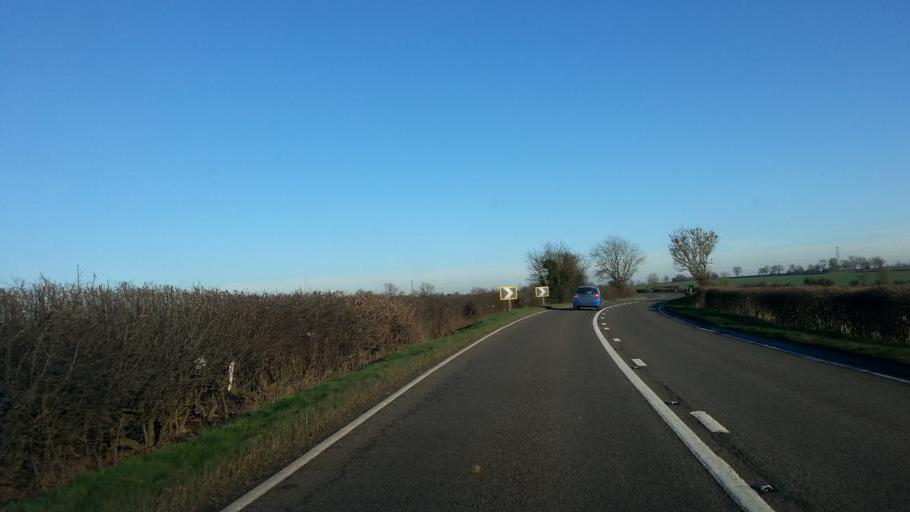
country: GB
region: England
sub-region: Leicestershire
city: Asfordby
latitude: 52.7441
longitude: -0.9762
